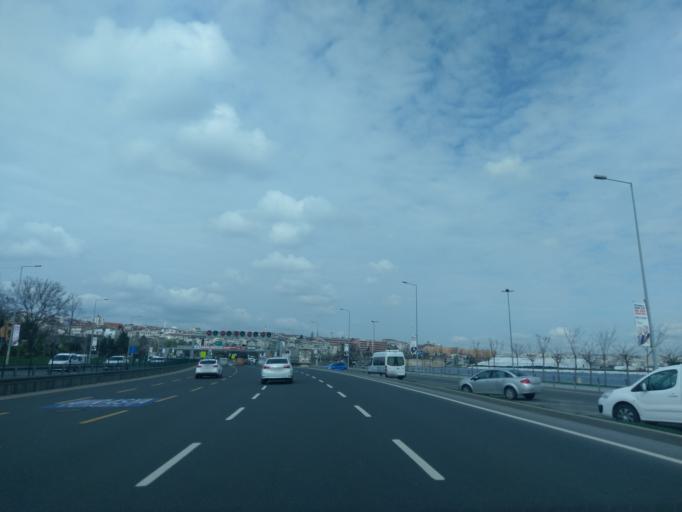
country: TR
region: Istanbul
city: Istanbul
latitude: 40.9962
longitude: 28.9327
